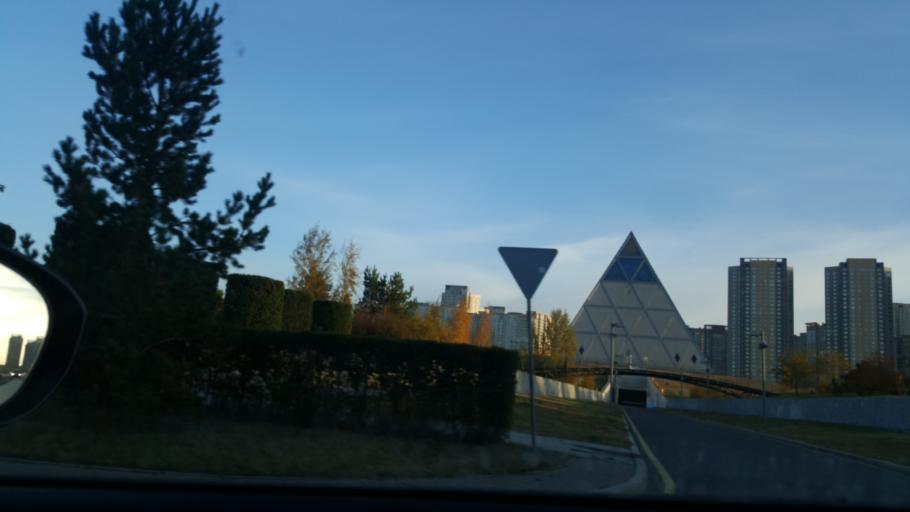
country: KZ
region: Astana Qalasy
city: Astana
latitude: 51.1211
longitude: 71.4646
